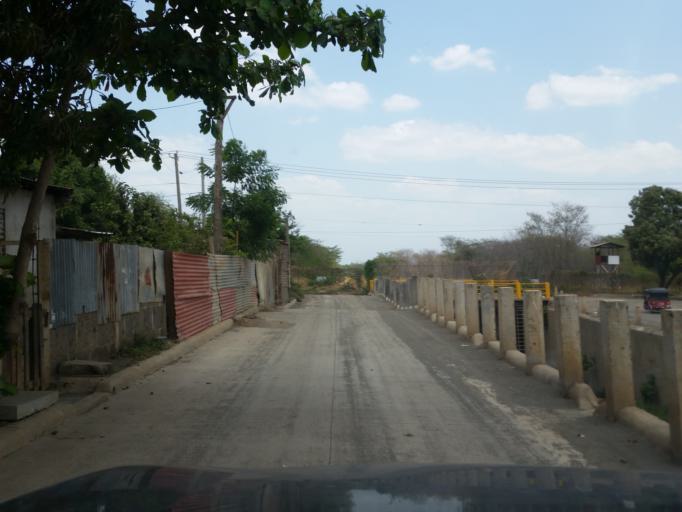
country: NI
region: Managua
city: Managua
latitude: 12.1371
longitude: -86.1882
